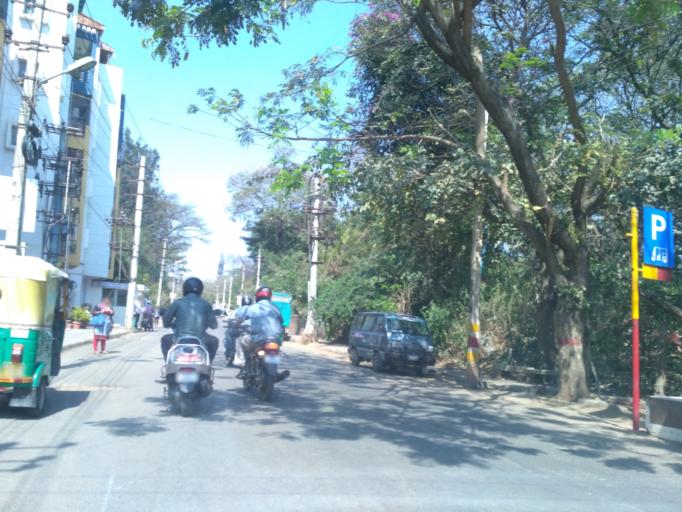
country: IN
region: Karnataka
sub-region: Bangalore Urban
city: Yelahanka
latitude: 13.0489
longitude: 77.5501
